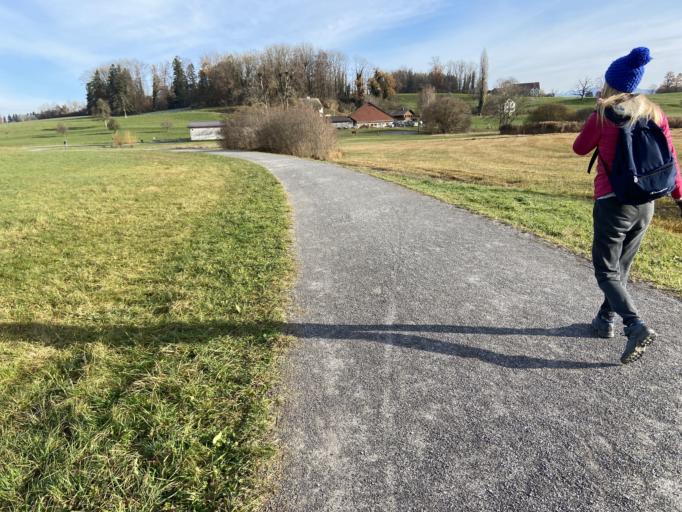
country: CH
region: Zurich
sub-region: Bezirk Meilen
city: Hombrechtikon
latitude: 47.2618
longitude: 8.7734
